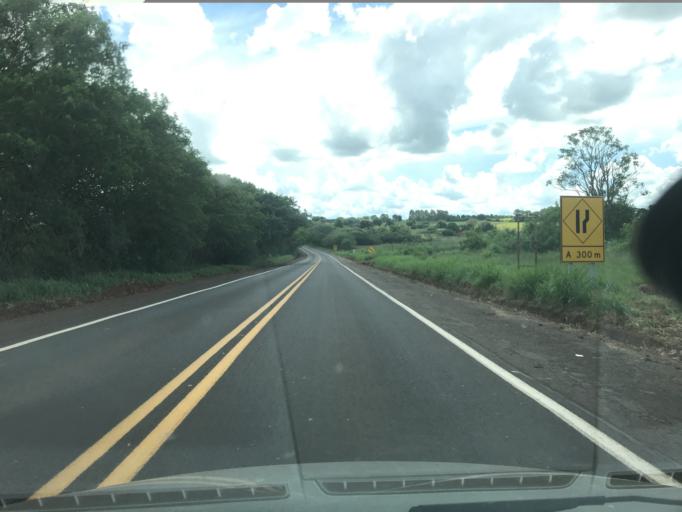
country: BR
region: Parana
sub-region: Cruzeiro Do Oeste
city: Cruzeiro do Oeste
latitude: -23.7891
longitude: -53.0306
